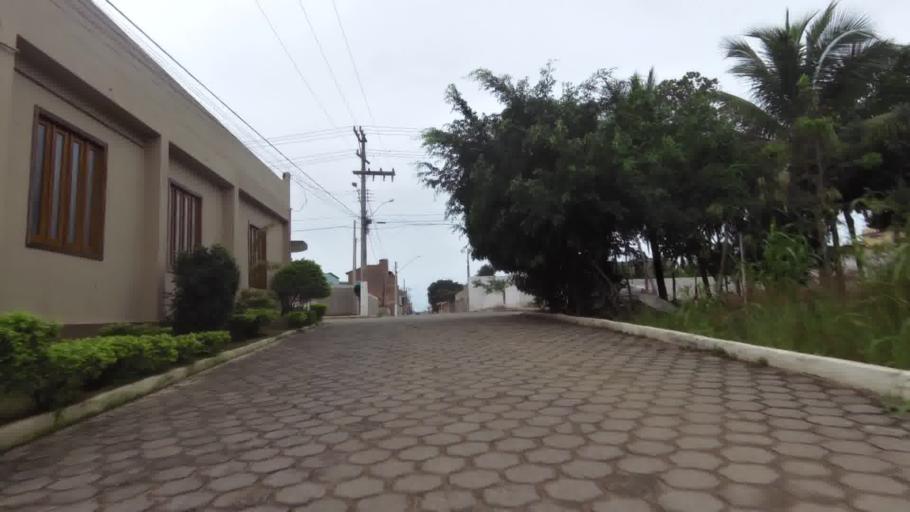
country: BR
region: Espirito Santo
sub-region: Marataizes
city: Marataizes
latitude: -21.0441
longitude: -40.8367
